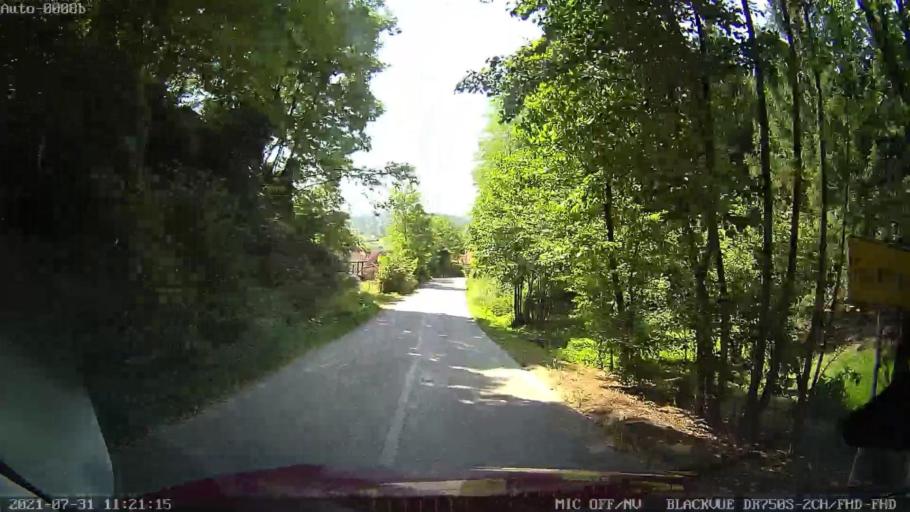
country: HR
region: Varazdinska
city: Jalzabet
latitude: 46.2280
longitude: 16.4744
